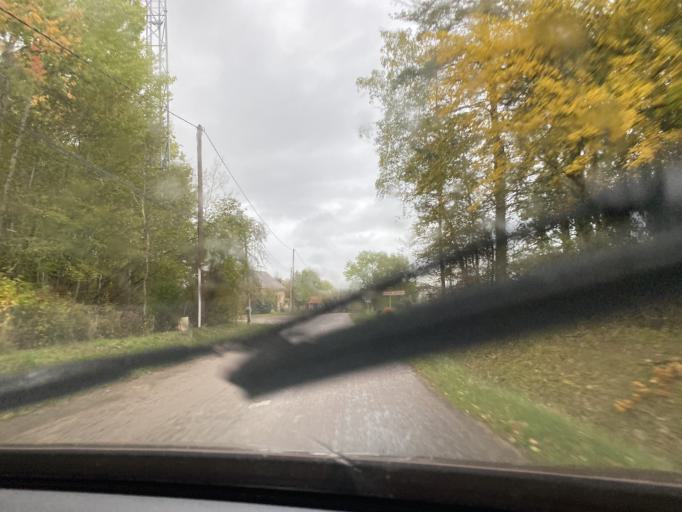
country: FR
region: Bourgogne
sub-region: Departement de la Cote-d'Or
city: Saulieu
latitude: 47.3564
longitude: 4.2449
